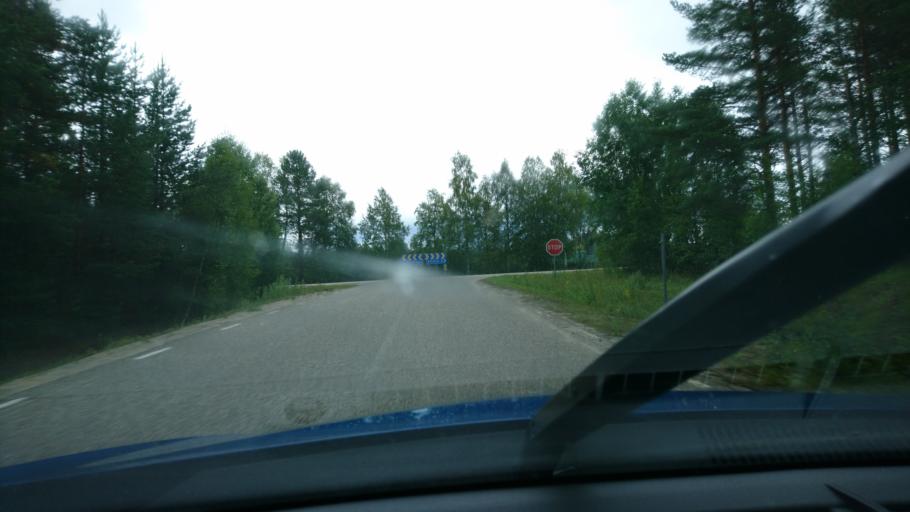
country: SE
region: Vaesterbotten
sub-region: Norsjo Kommun
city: Norsjoe
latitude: 64.5793
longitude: 19.3025
